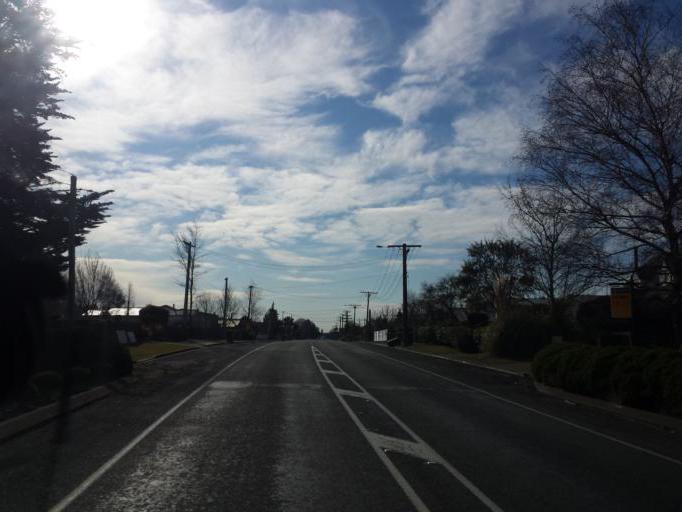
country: NZ
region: Canterbury
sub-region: Timaru District
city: Pleasant Point
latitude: -44.1025
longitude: 171.2377
